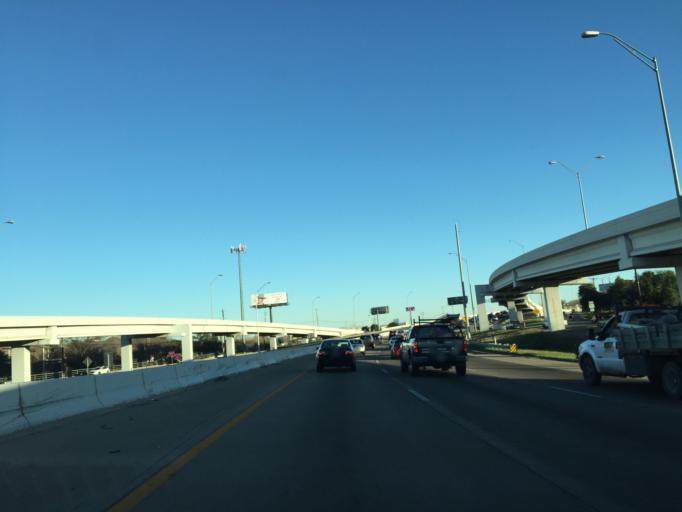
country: US
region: Texas
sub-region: Travis County
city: Wells Branch
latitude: 30.3705
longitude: -97.7208
